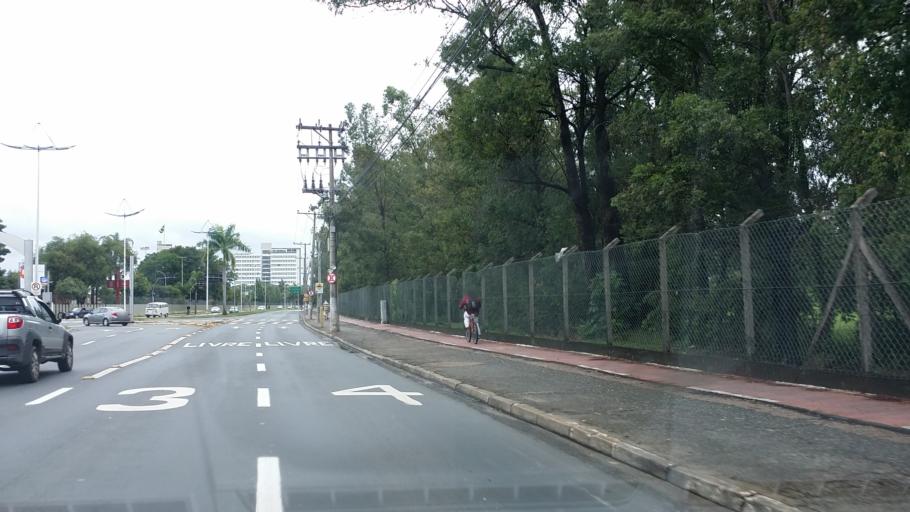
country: BR
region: Sao Paulo
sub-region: Indaiatuba
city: Indaiatuba
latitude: -23.1112
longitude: -47.2201
